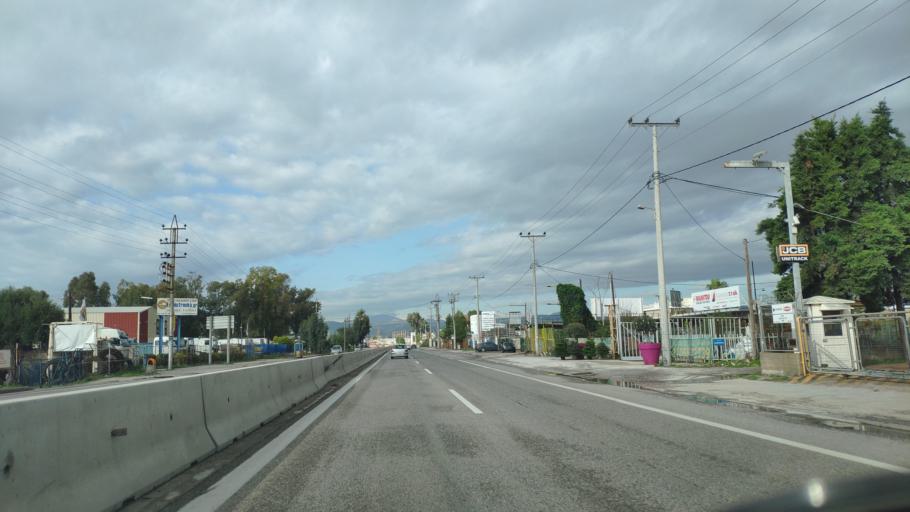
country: GR
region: Attica
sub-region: Nomarchia Dytikis Attikis
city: Aspropyrgos
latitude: 38.0458
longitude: 23.5790
